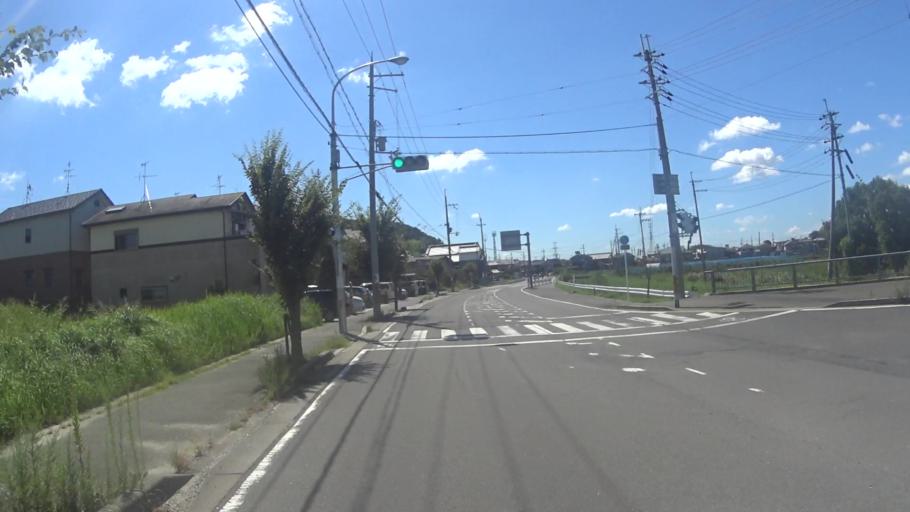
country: JP
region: Nara
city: Nara-shi
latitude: 34.7368
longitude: 135.8536
